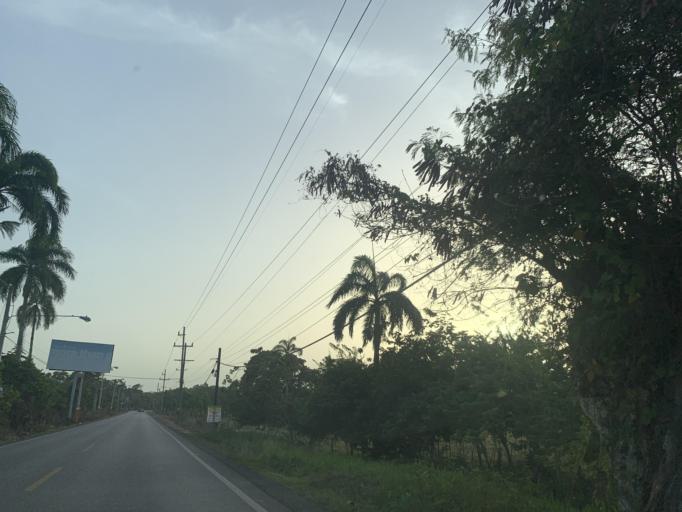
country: DO
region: Puerto Plata
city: Cabarete
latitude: 19.7752
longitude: -70.4574
